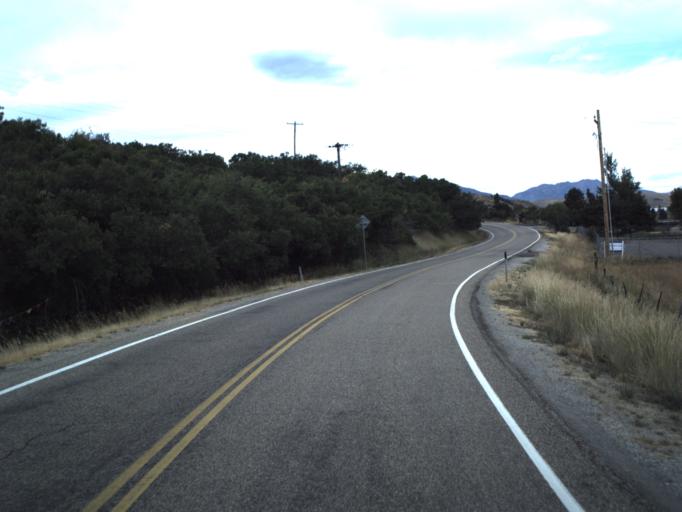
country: US
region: Utah
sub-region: Morgan County
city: Morgan
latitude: 40.9519
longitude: -111.6613
